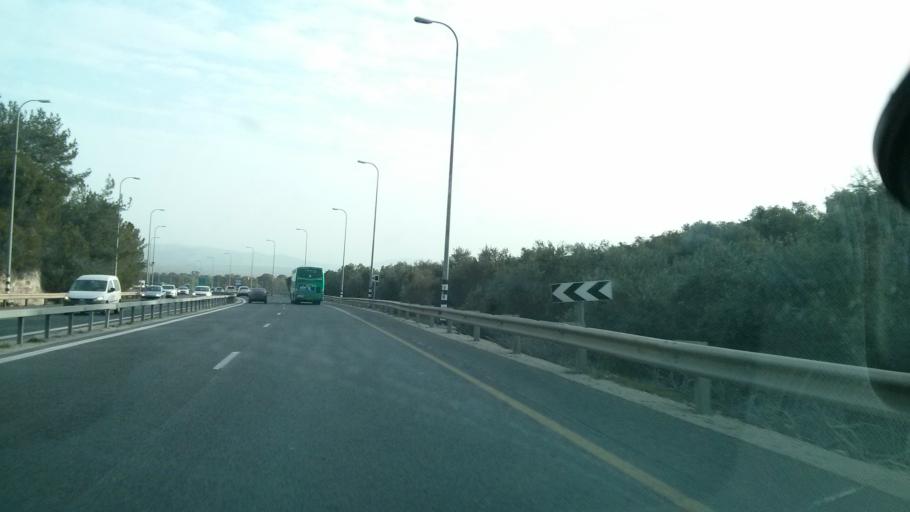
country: PS
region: West Bank
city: Rummanah
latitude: 32.5643
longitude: 35.1766
